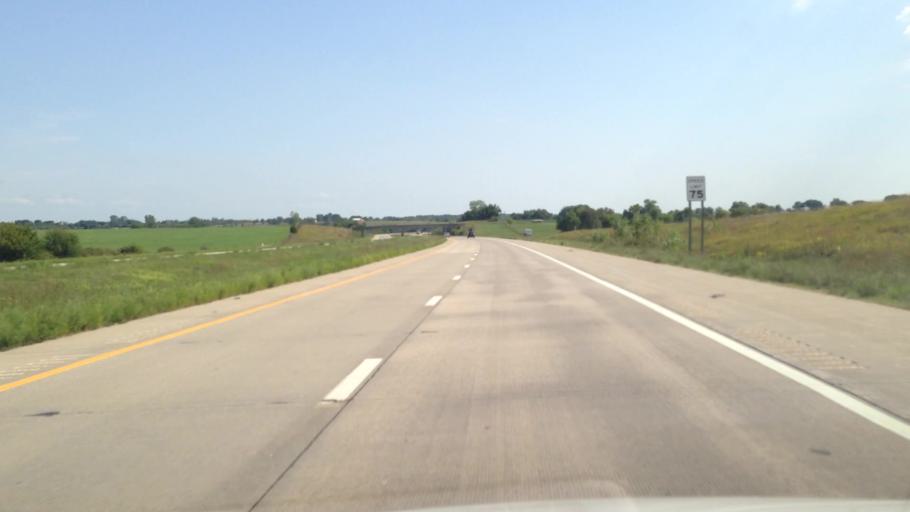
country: US
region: Kansas
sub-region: Miami County
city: Louisburg
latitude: 38.5542
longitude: -94.6906
